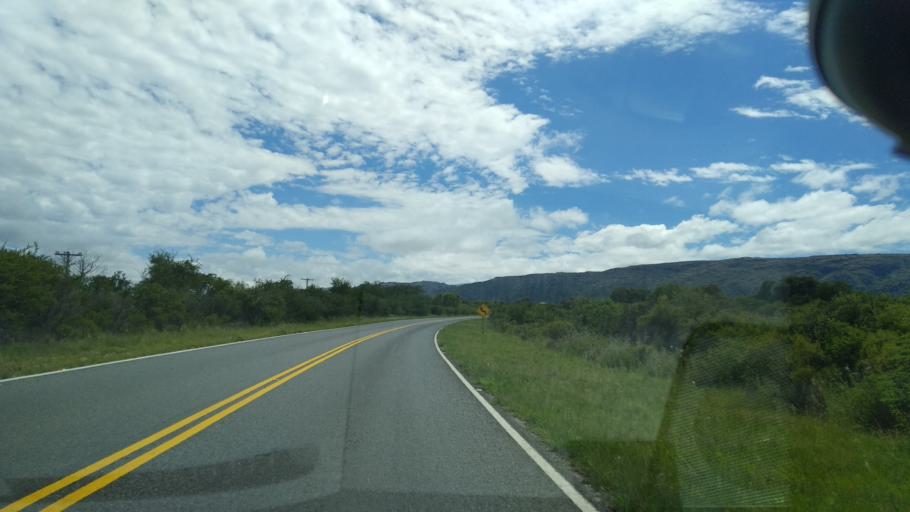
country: AR
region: Cordoba
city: Mina Clavero
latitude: -31.7492
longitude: -64.9509
